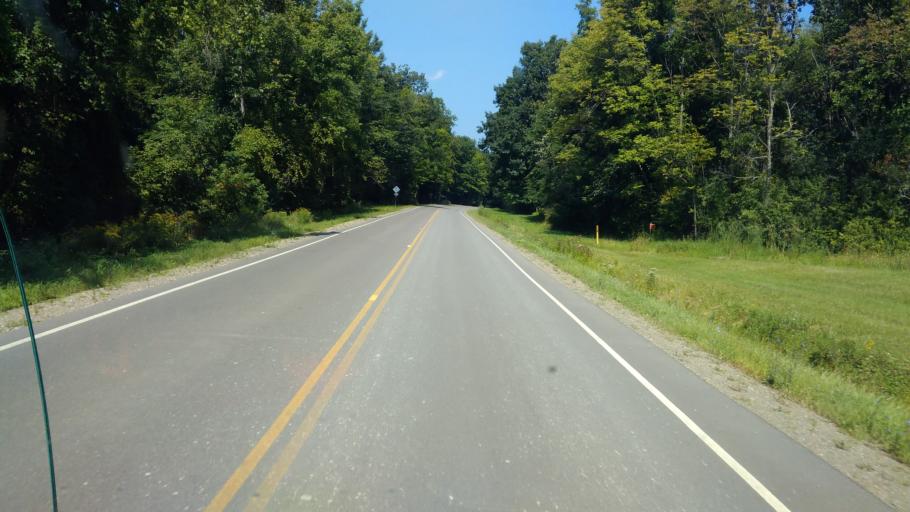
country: US
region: New York
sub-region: Allegany County
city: Belmont
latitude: 42.2624
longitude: -78.0392
